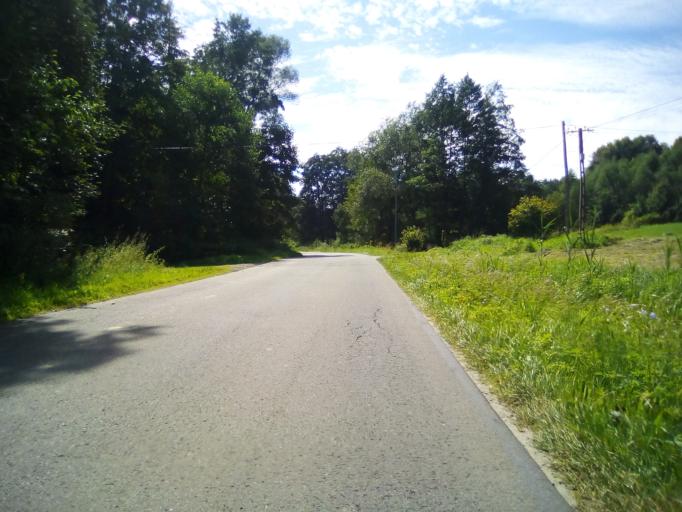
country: PL
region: Subcarpathian Voivodeship
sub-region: Powiat strzyzowski
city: Konieczkowa
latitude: 49.8282
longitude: 21.9284
